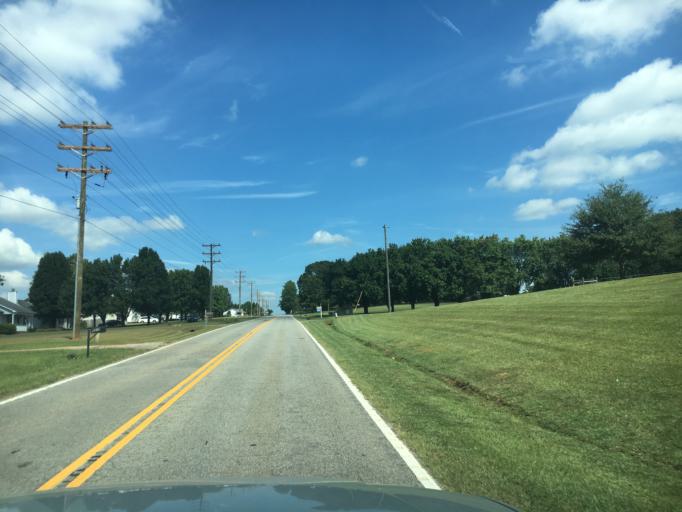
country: US
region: South Carolina
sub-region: Spartanburg County
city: Boiling Springs
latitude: 35.0741
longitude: -81.9291
